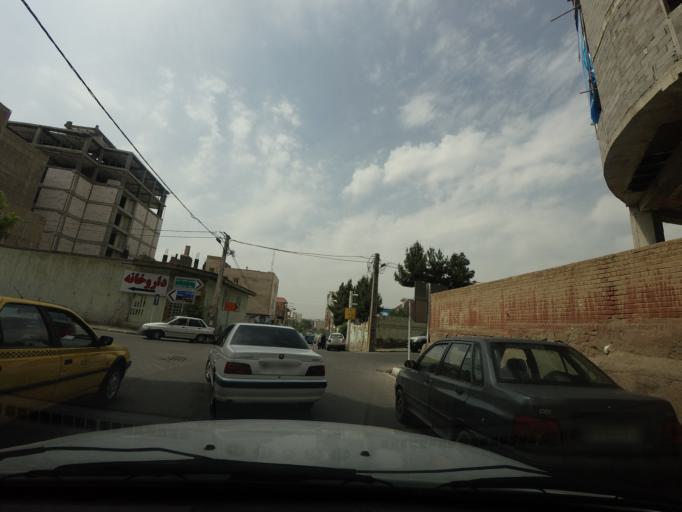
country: IR
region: Tehran
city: Shahr-e Qods
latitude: 35.7546
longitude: 51.0703
